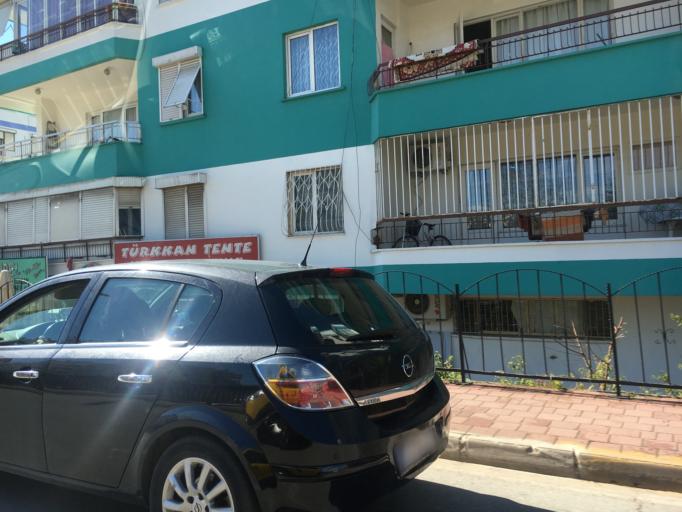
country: TR
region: Antalya
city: Antalya
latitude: 36.8960
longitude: 30.7141
